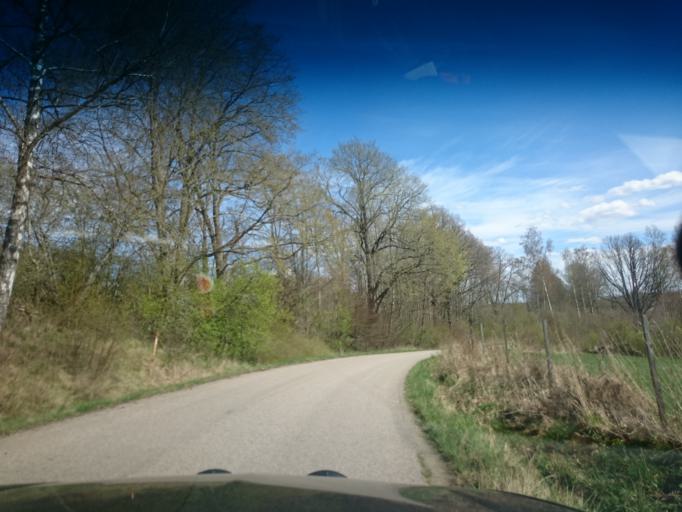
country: SE
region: Kronoberg
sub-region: Uppvidinge Kommun
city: Aseda
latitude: 57.3706
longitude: 15.3858
